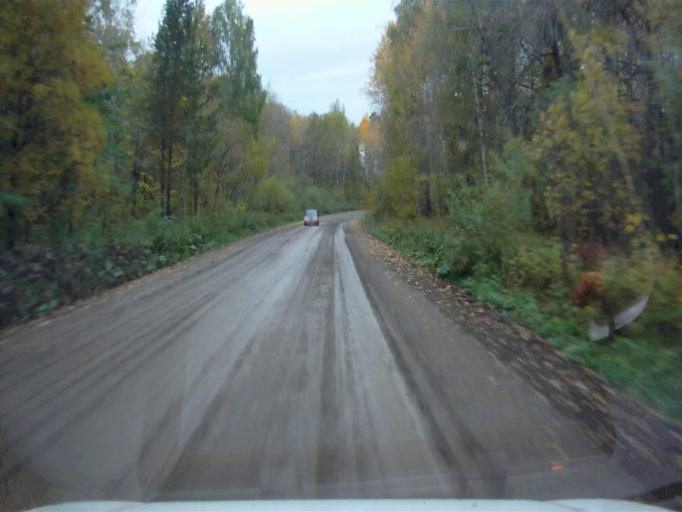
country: RU
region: Chelyabinsk
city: Nyazepetrovsk
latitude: 56.1141
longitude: 59.3686
